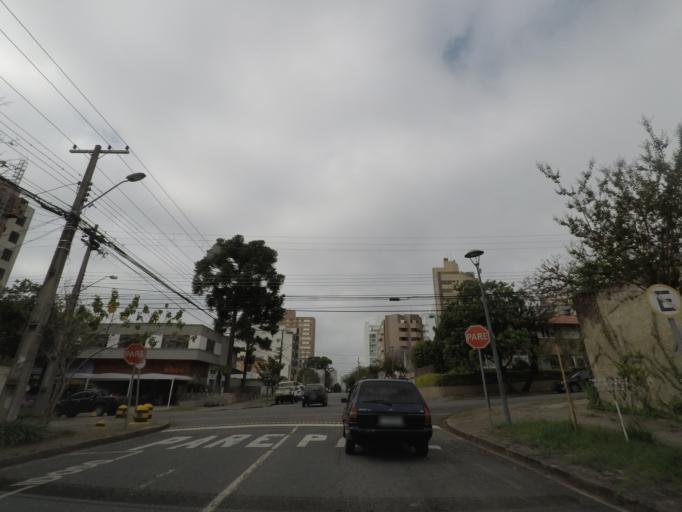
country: BR
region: Parana
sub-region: Curitiba
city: Curitiba
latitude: -25.4315
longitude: -49.2874
